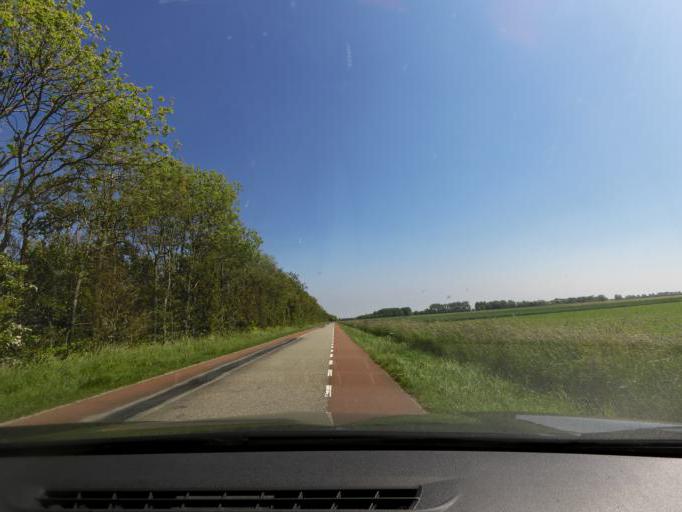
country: NL
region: South Holland
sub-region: Gemeente Goeree-Overflakkee
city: Dirksland
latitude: 51.7850
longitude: 4.0445
